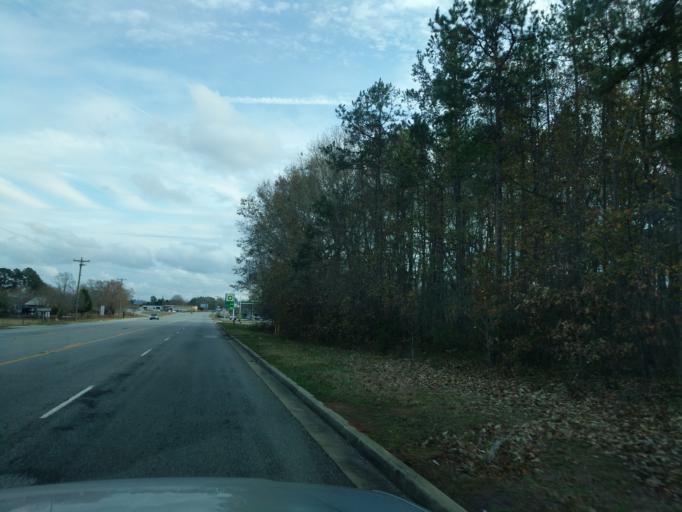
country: US
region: South Carolina
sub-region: Anderson County
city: Honea Path
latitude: 34.5038
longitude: -82.2937
